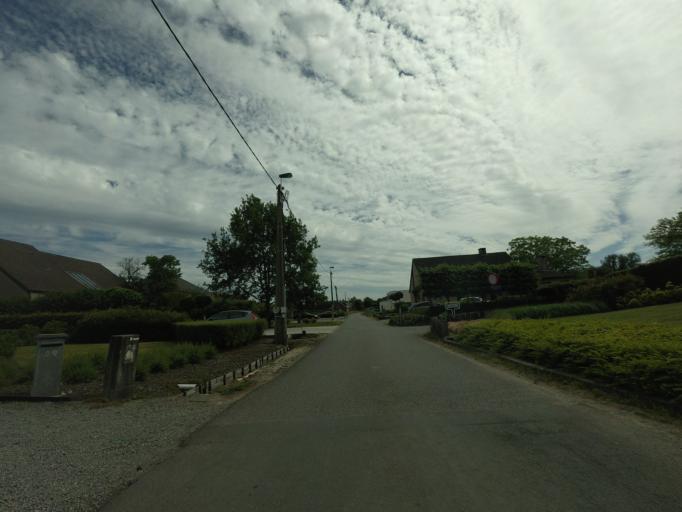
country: BE
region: Flanders
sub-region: Provincie Antwerpen
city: Rumst
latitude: 51.0845
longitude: 4.4646
